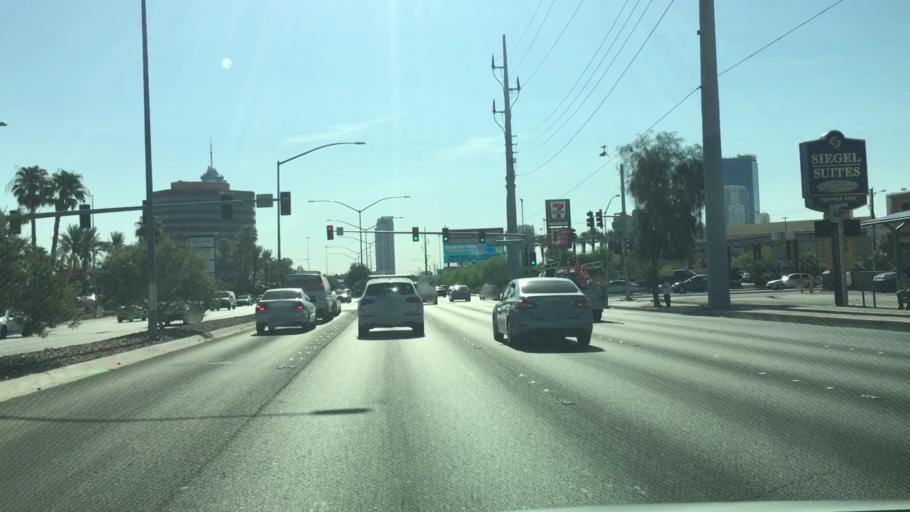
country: US
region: Nevada
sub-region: Clark County
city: Las Vegas
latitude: 36.1443
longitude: -115.1783
